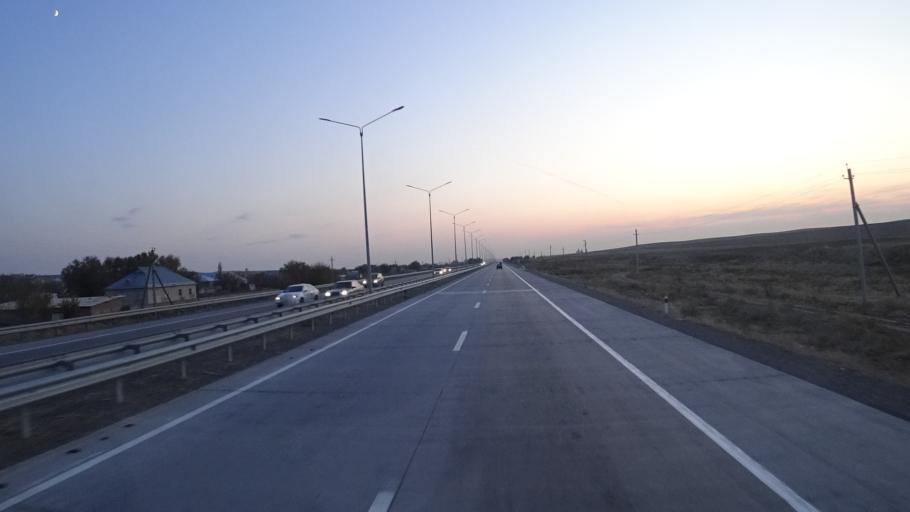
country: KZ
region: Ongtustik Qazaqstan
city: Qazyqurt
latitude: 41.8910
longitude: 69.4477
